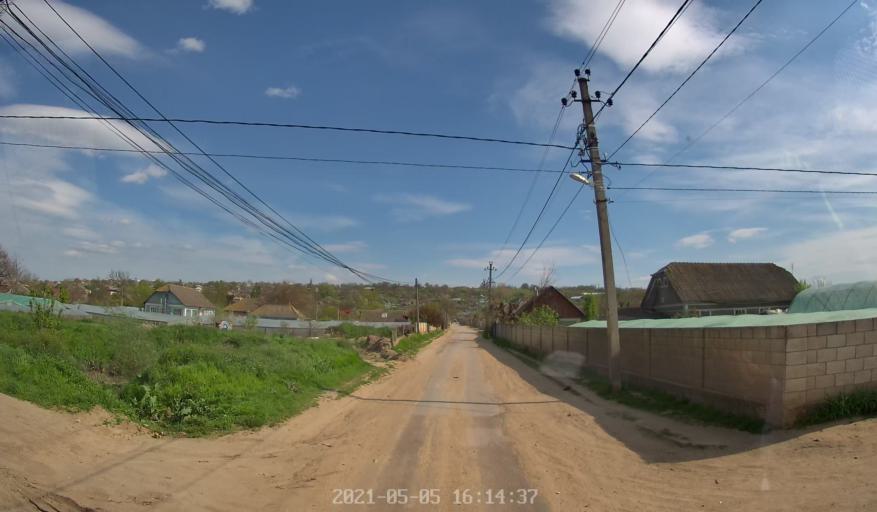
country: MD
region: Criuleni
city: Criuleni
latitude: 47.1366
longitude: 29.2012
